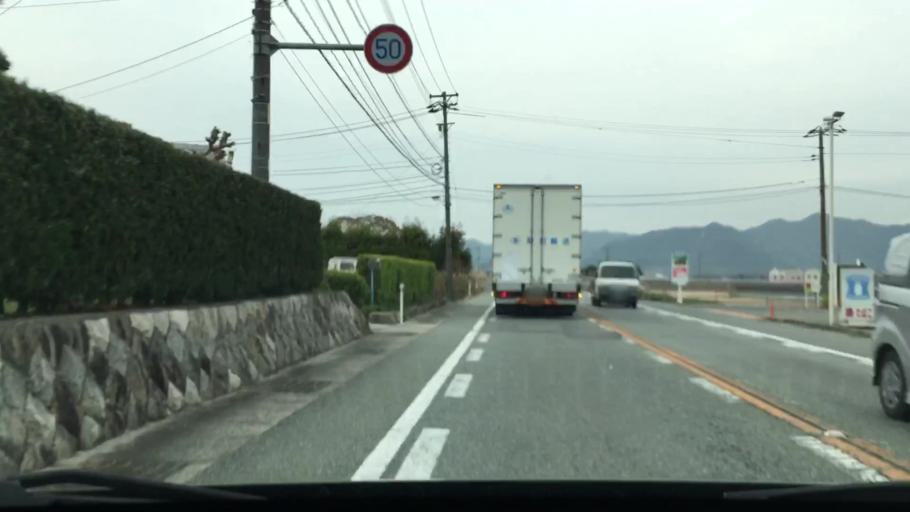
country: JP
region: Yamaguchi
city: Ogori-shimogo
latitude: 34.0711
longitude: 131.4617
